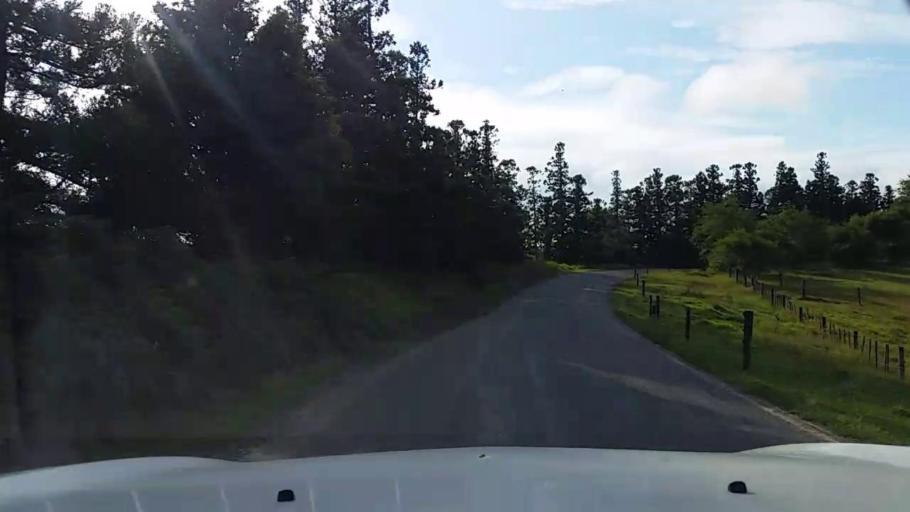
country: NZ
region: Northland
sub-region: Whangarei
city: Maungatapere
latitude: -35.6777
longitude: 174.1780
